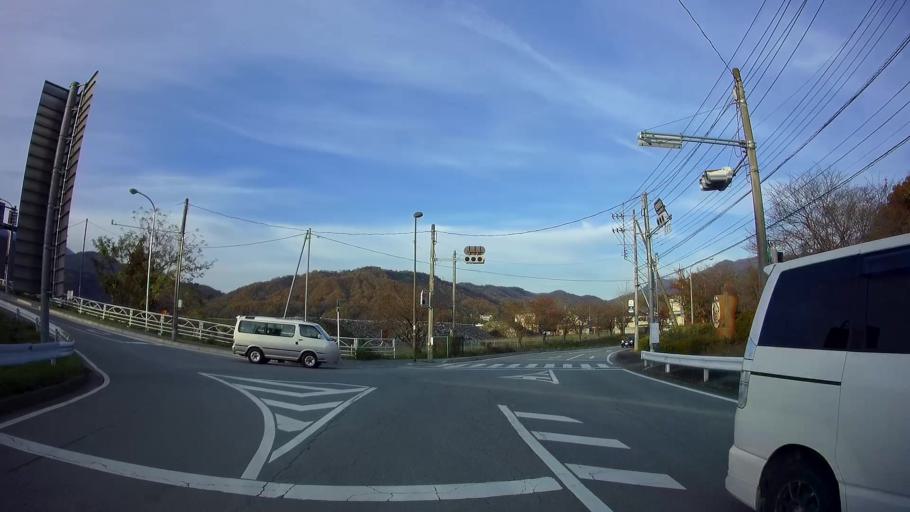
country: JP
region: Yamanashi
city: Ryuo
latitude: 35.4839
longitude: 138.4560
